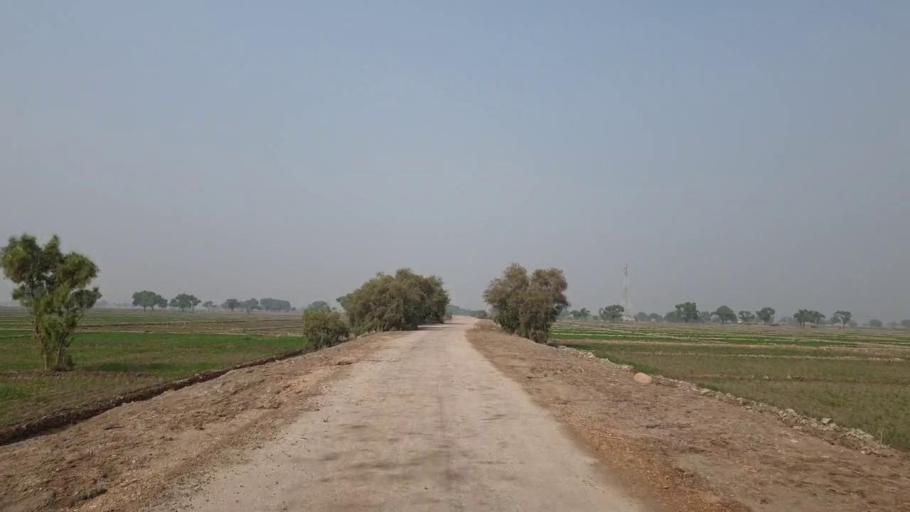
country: PK
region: Sindh
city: Bhan
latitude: 26.4933
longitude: 67.6995
